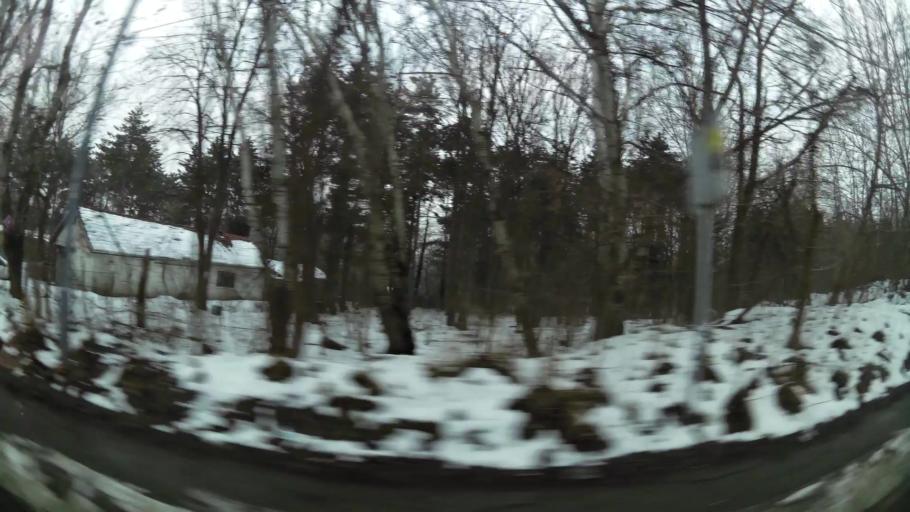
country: RS
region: Central Serbia
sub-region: Belgrade
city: Vozdovac
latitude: 44.7720
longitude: 20.4991
